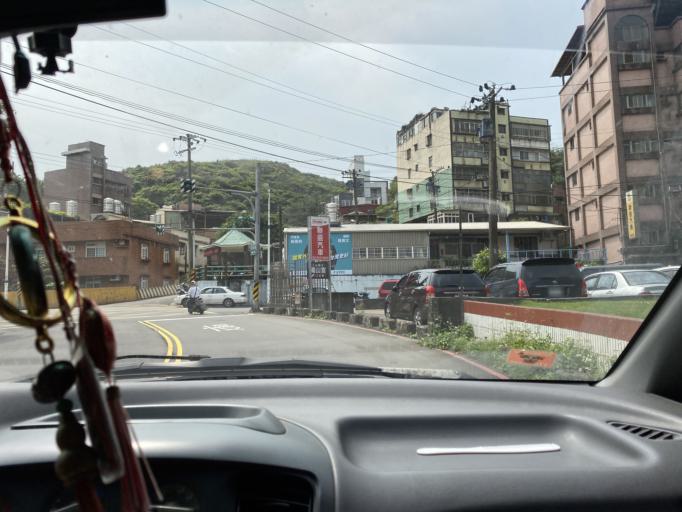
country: TW
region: Taiwan
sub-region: Keelung
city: Keelung
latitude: 25.1564
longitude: 121.7302
